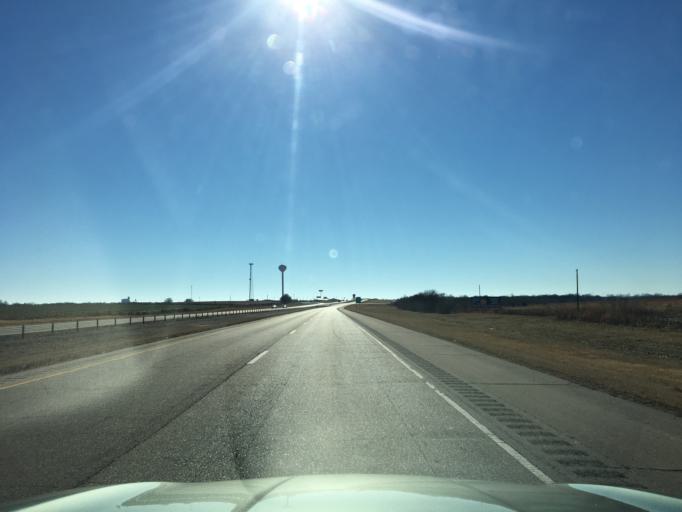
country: US
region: Oklahoma
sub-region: Kay County
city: Blackwell
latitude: 36.9498
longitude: -97.3458
